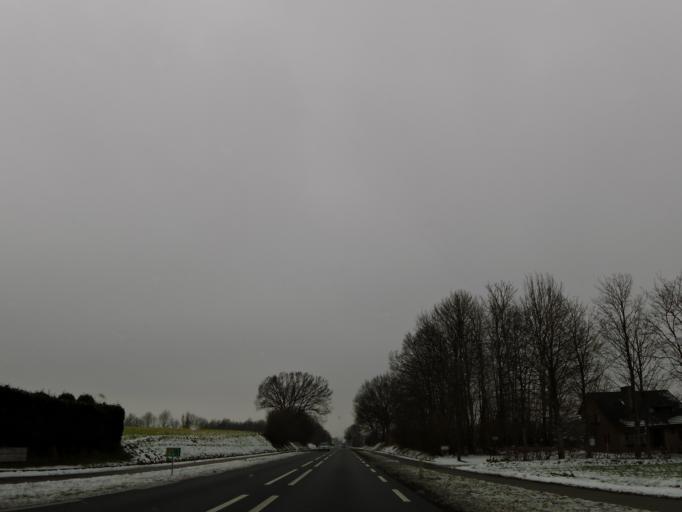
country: NL
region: Limburg
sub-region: Gemeente Vaals
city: Vaals
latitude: 50.7894
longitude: 5.9867
